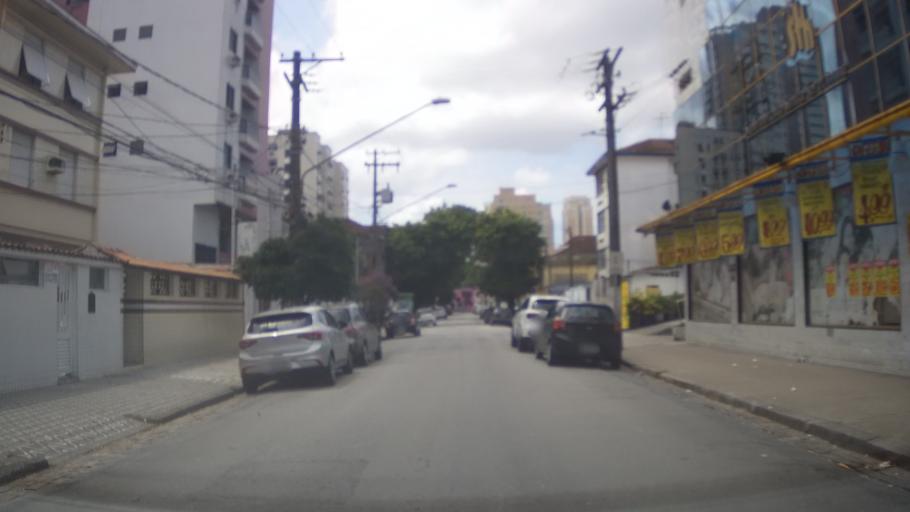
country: BR
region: Sao Paulo
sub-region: Santos
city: Santos
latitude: -23.9618
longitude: -46.3438
